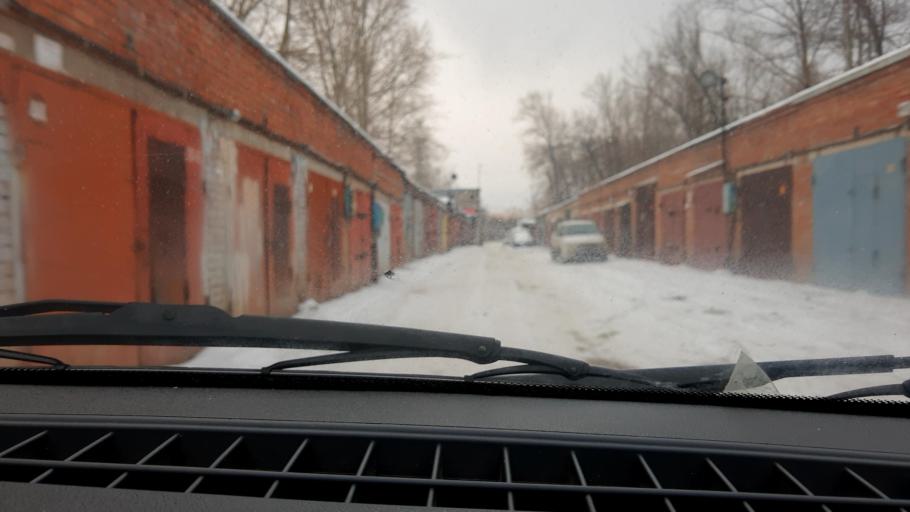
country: RU
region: Bashkortostan
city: Ufa
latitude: 54.7937
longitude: 56.1143
